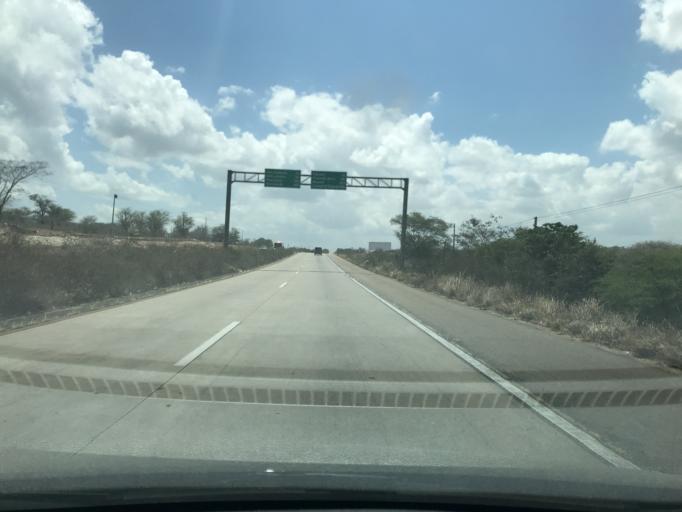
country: BR
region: Pernambuco
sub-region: Bezerros
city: Bezerros
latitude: -8.2983
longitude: -35.8597
